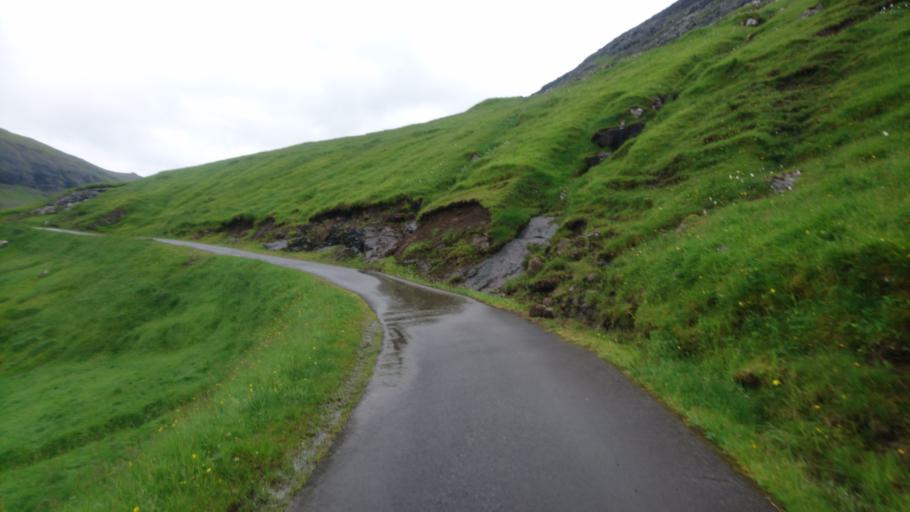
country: FO
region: Streymoy
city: Vestmanna
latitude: 62.2437
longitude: -7.1768
